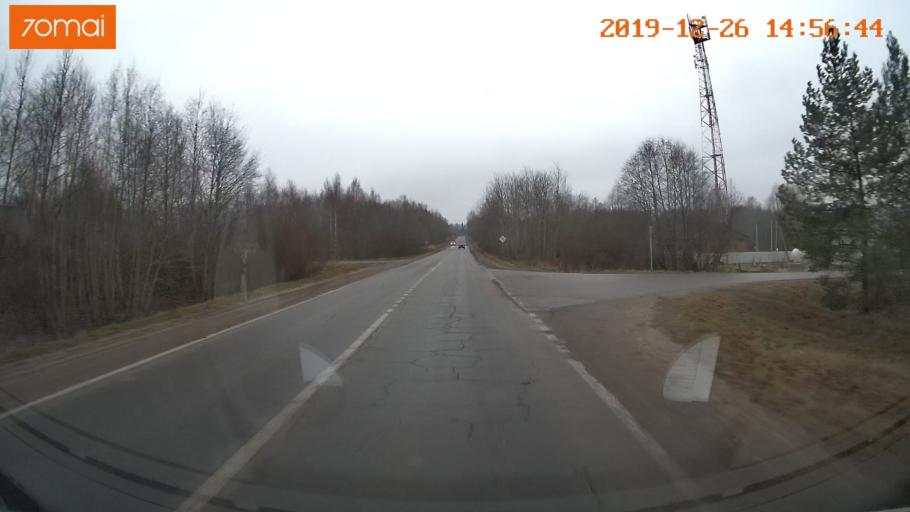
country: RU
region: Jaroslavl
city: Rybinsk
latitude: 58.2897
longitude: 38.8696
